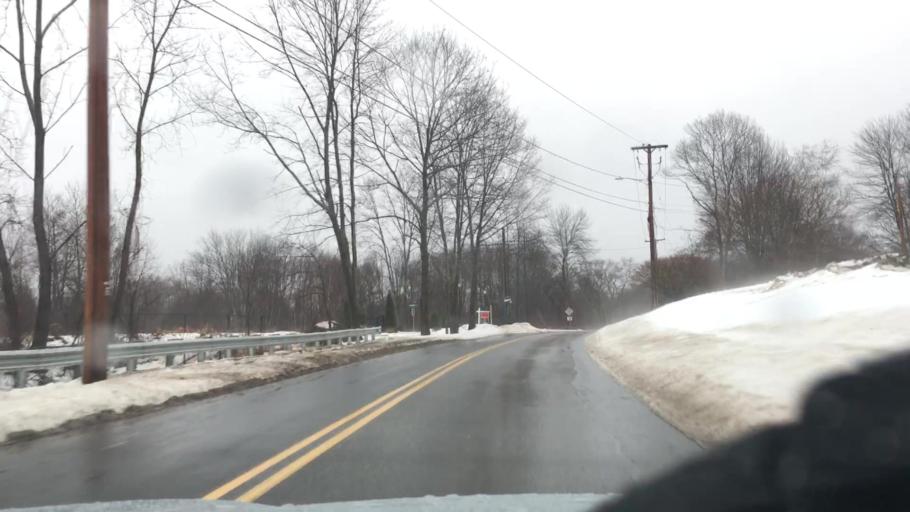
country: US
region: Massachusetts
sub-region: Hampshire County
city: Belchertown
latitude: 42.2870
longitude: -72.4170
